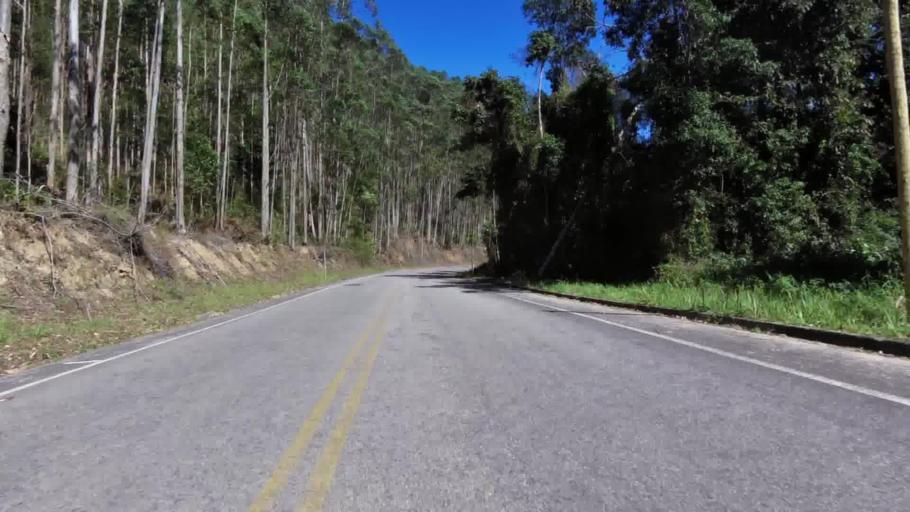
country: BR
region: Espirito Santo
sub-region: Vargem Alta
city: Vargem Alta
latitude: -20.6844
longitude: -40.9477
